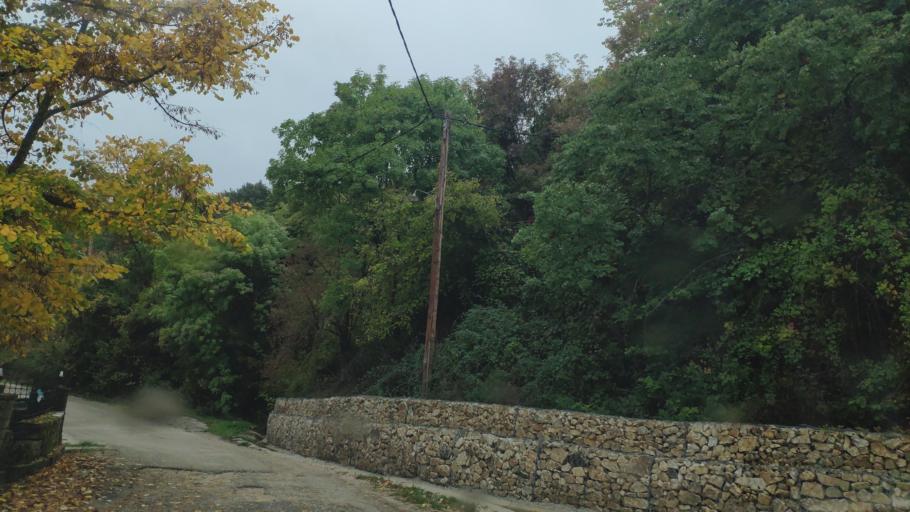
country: GR
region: Epirus
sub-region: Nomos Thesprotias
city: Paramythia
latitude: 39.4597
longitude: 20.6722
